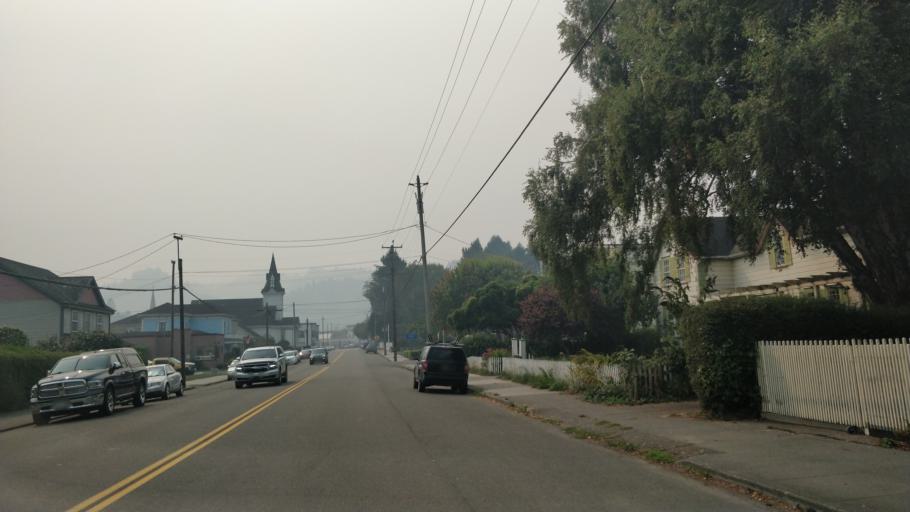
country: US
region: California
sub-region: Humboldt County
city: Ferndale
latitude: 40.5802
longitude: -124.2606
